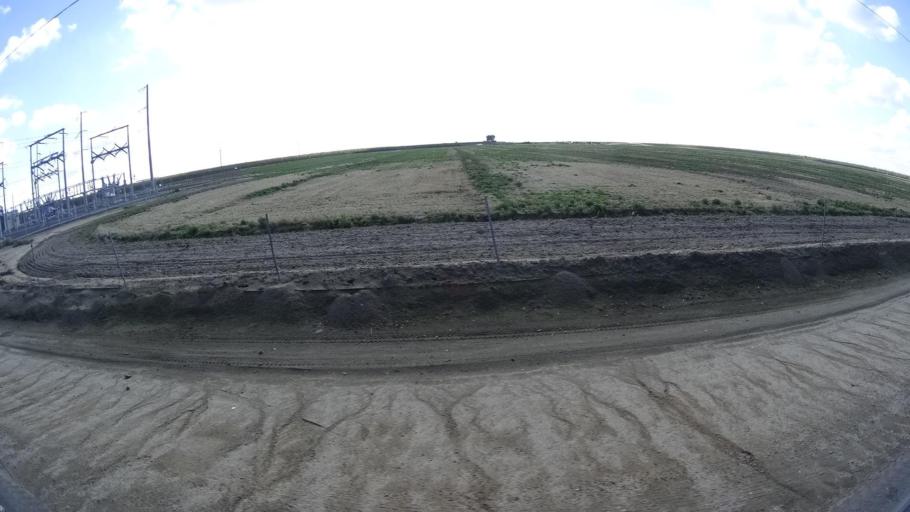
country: US
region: California
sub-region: Kern County
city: McFarland
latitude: 35.6887
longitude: -119.2777
